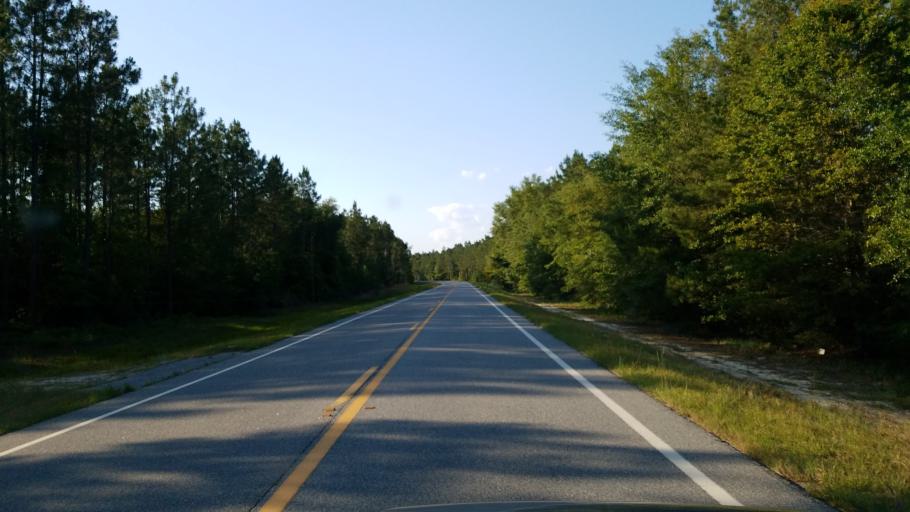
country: US
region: Georgia
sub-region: Lanier County
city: Lakeland
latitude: 30.8831
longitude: -83.0531
